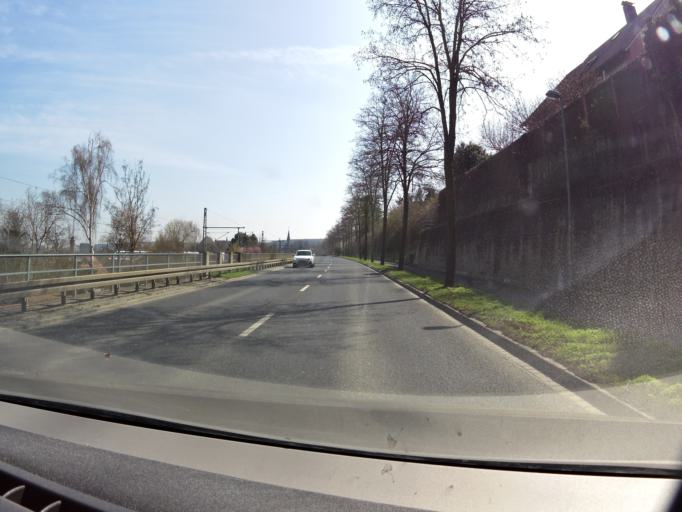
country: DE
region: Bavaria
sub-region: Regierungsbezirk Unterfranken
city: Ochsenfurt
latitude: 49.6660
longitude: 10.0527
